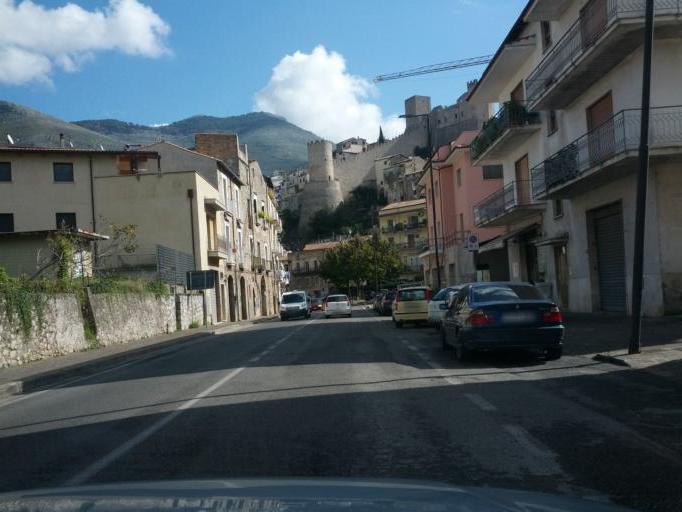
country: IT
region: Latium
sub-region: Provincia di Latina
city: Itri
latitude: 41.2896
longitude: 13.5279
